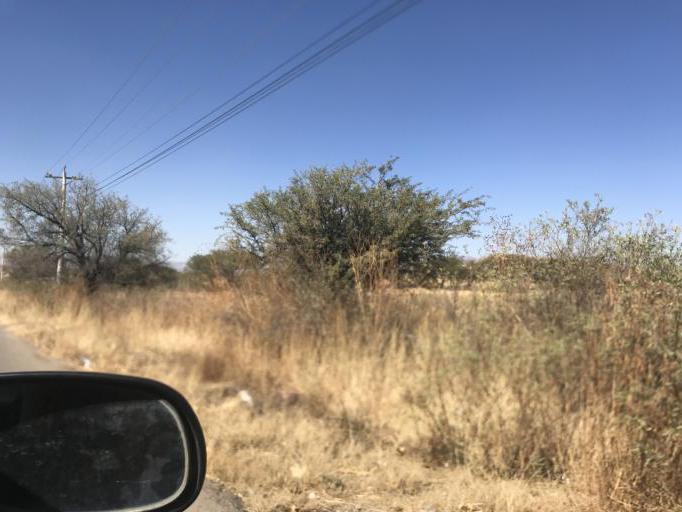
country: BO
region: Cochabamba
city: Cliza
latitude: -17.5992
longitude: -65.9626
